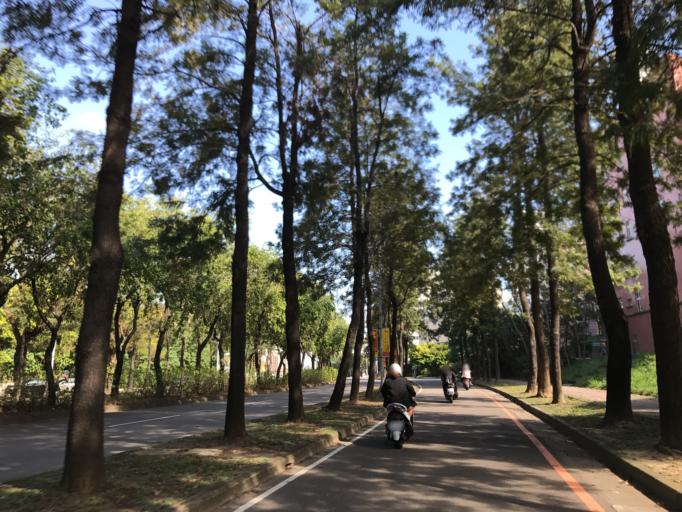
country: TW
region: Taiwan
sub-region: Hsinchu
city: Hsinchu
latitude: 24.7772
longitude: 121.0182
